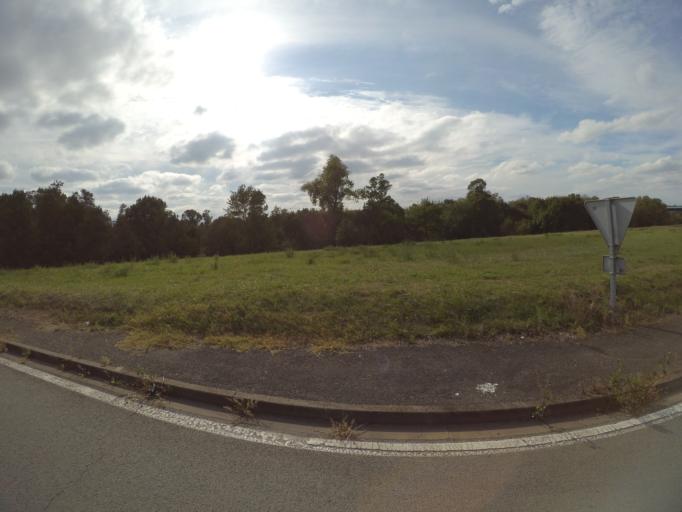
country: FR
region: Centre
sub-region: Departement d'Indre-et-Loire
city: Vouvray
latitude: 47.4038
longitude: 0.8063
